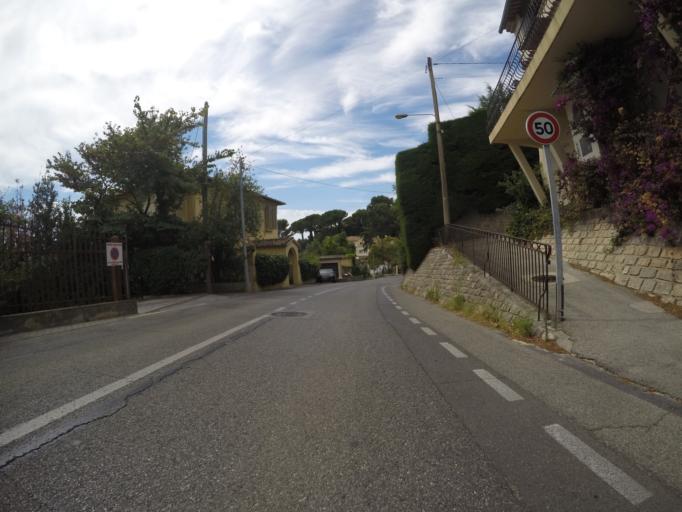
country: FR
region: Provence-Alpes-Cote d'Azur
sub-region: Departement des Alpes-Maritimes
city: Mougins
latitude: 43.6004
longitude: 6.9964
